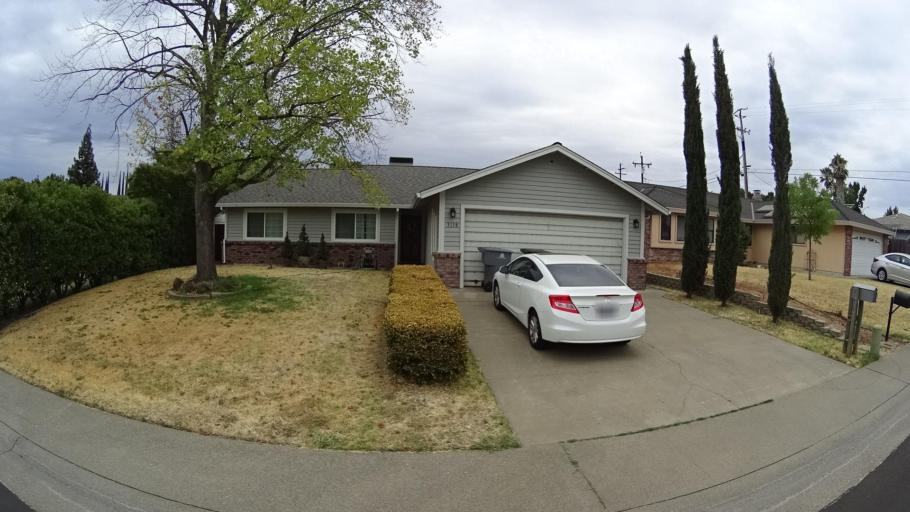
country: US
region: California
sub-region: Placer County
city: Rocklin
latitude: 38.7732
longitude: -121.2454
